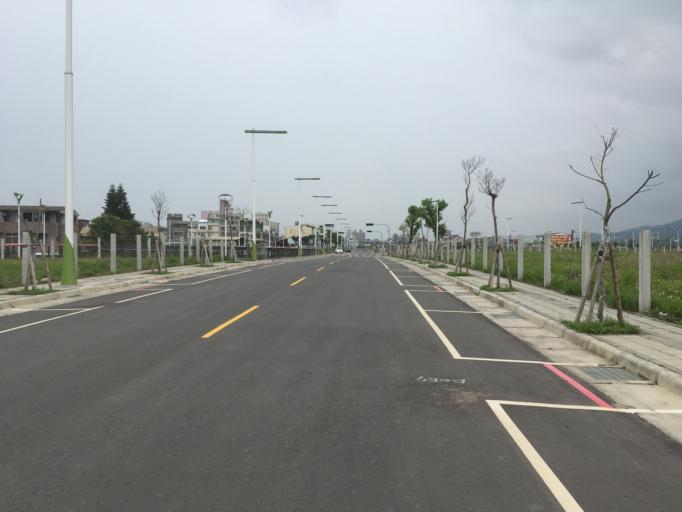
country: TW
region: Taiwan
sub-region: Taichung City
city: Taichung
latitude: 24.1882
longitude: 120.7050
